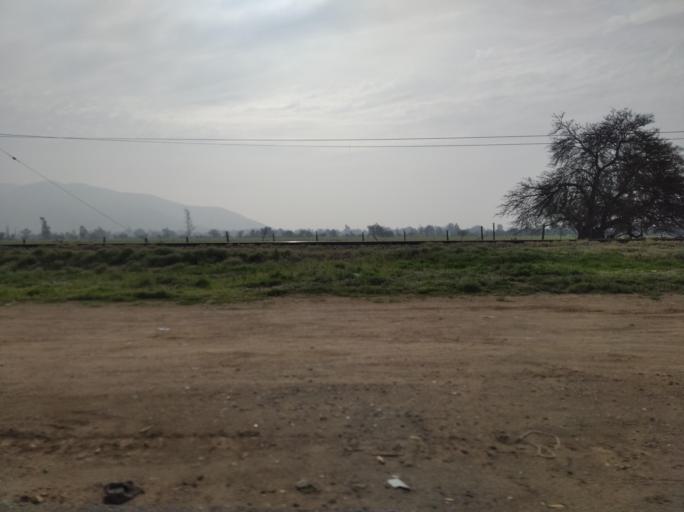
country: CL
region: Santiago Metropolitan
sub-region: Provincia de Chacabuco
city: Lampa
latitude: -33.1616
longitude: -70.8950
